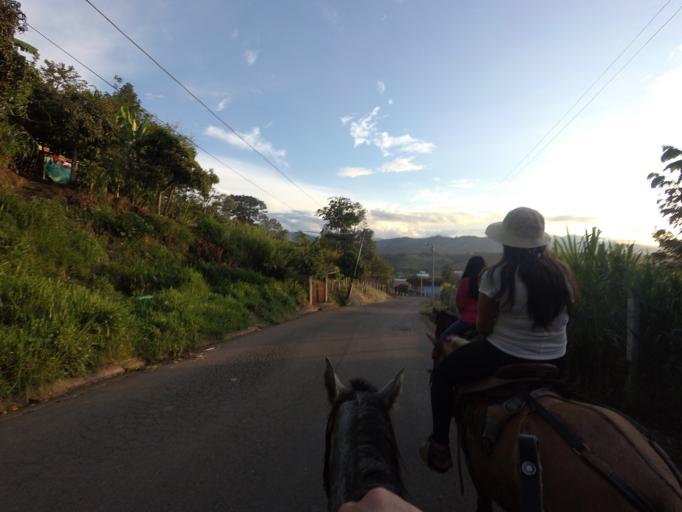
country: CO
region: Huila
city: San Agustin
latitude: 1.8886
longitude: -76.2720
